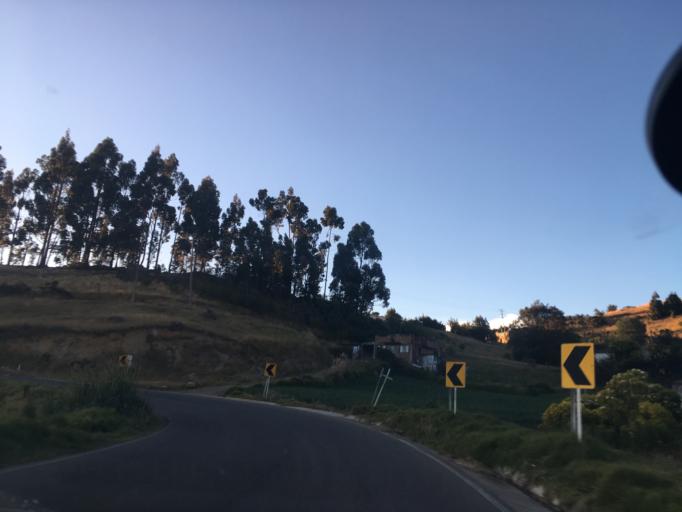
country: CO
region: Boyaca
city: Aquitania
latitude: 5.5623
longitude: -72.8814
